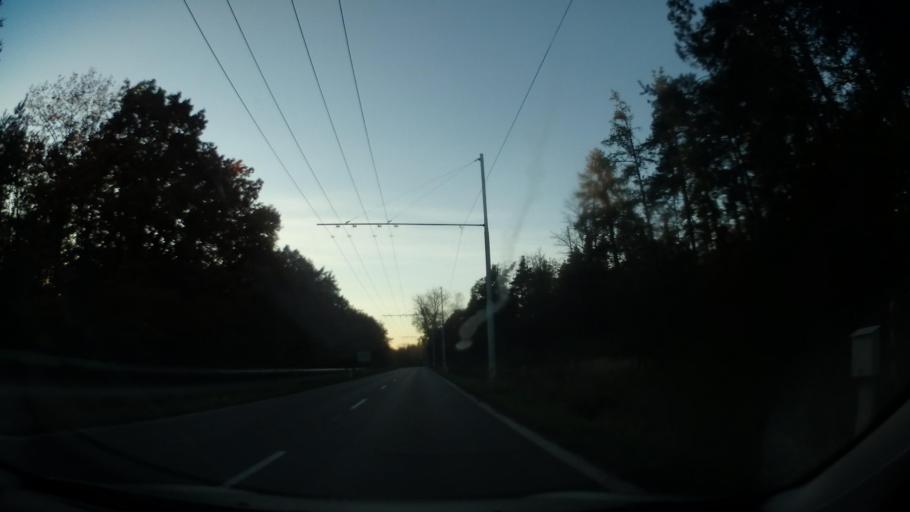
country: CZ
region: Pardubicky
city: Rybitvi
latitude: 50.0696
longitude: 15.6944
